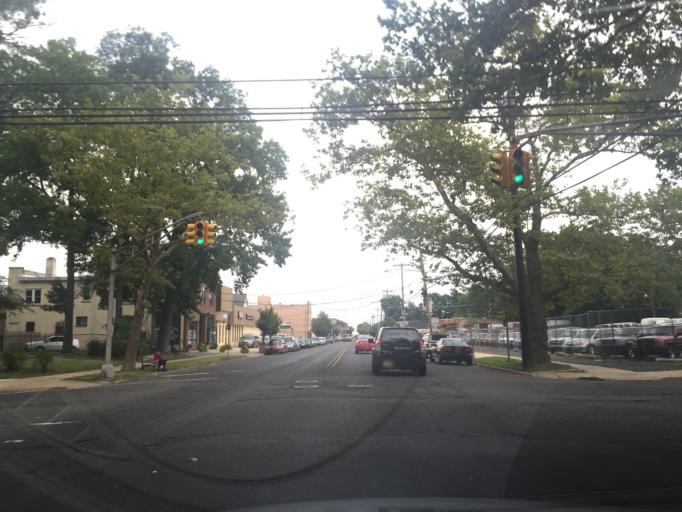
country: US
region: New Jersey
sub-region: Monmouth County
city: Asbury Park
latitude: 40.2214
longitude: -74.0170
